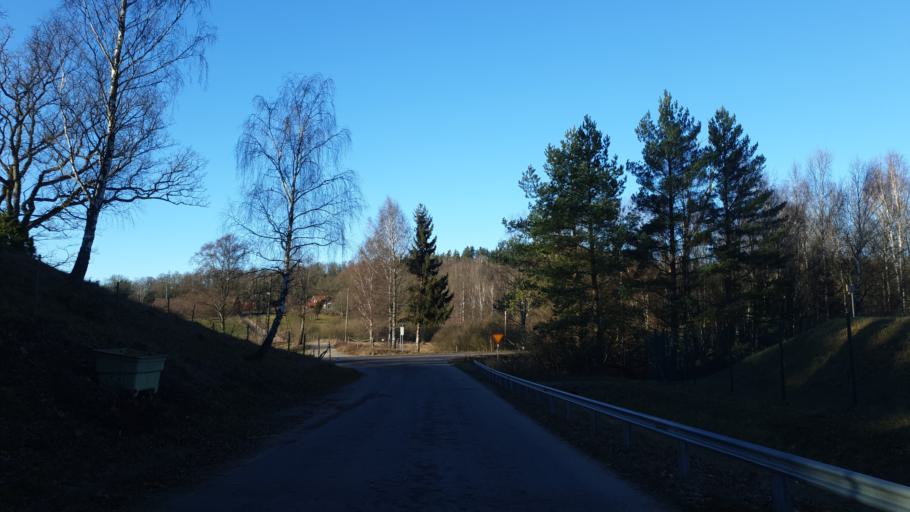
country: SE
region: Blekinge
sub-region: Karlskrona Kommun
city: Nattraby
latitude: 56.2620
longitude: 15.4284
